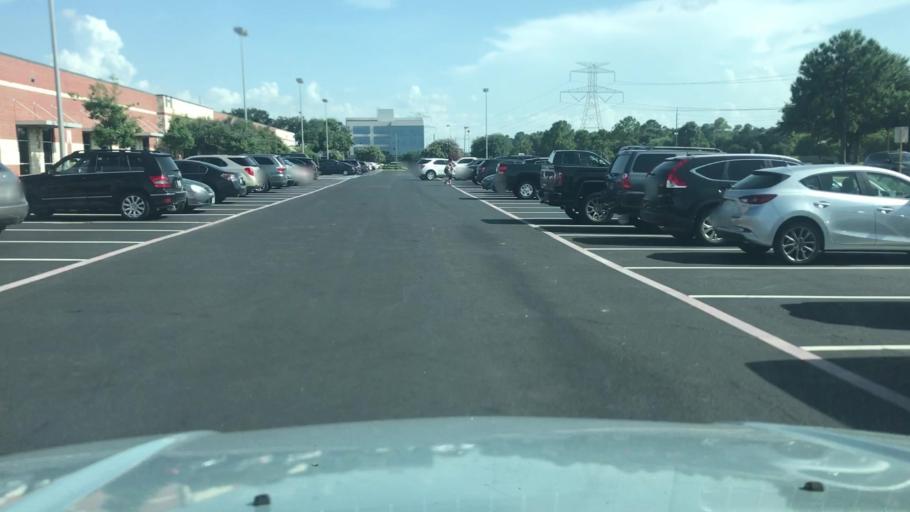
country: US
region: Texas
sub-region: Fort Bend County
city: Cinco Ranch
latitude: 29.7999
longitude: -95.7516
